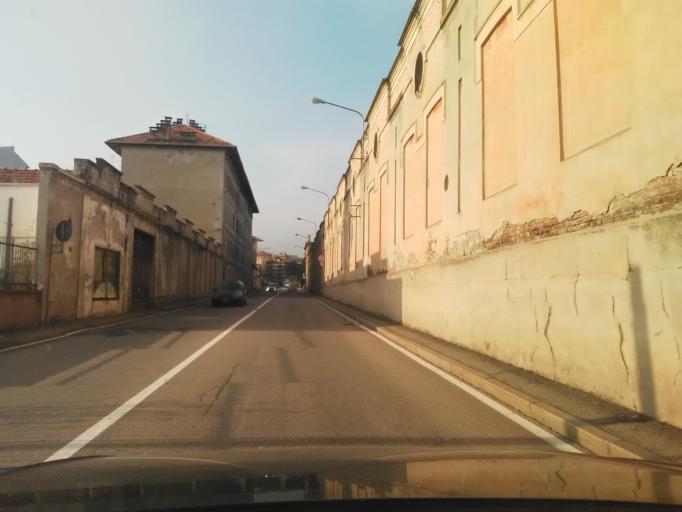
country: IT
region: Piedmont
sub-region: Provincia di Biella
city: Biella
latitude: 45.5620
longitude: 8.0627
